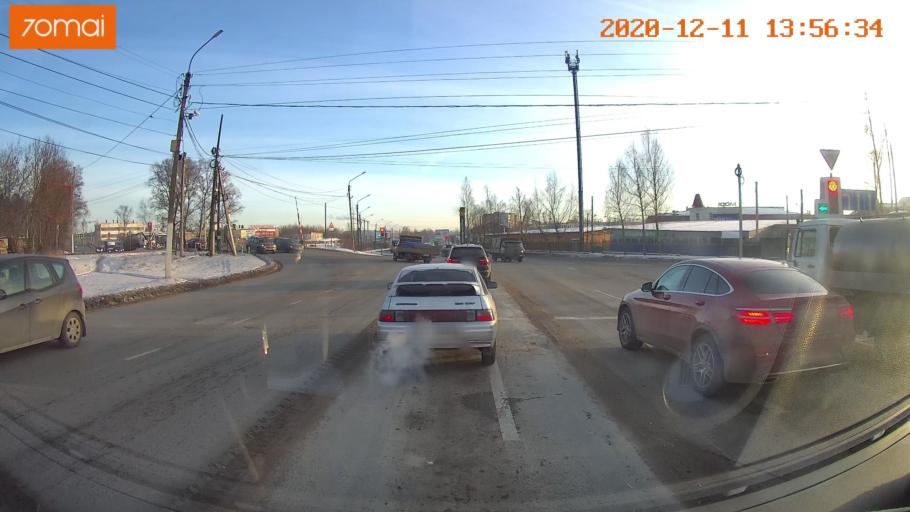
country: RU
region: Kostroma
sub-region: Kostromskoy Rayon
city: Kostroma
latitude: 57.7799
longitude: 40.9687
